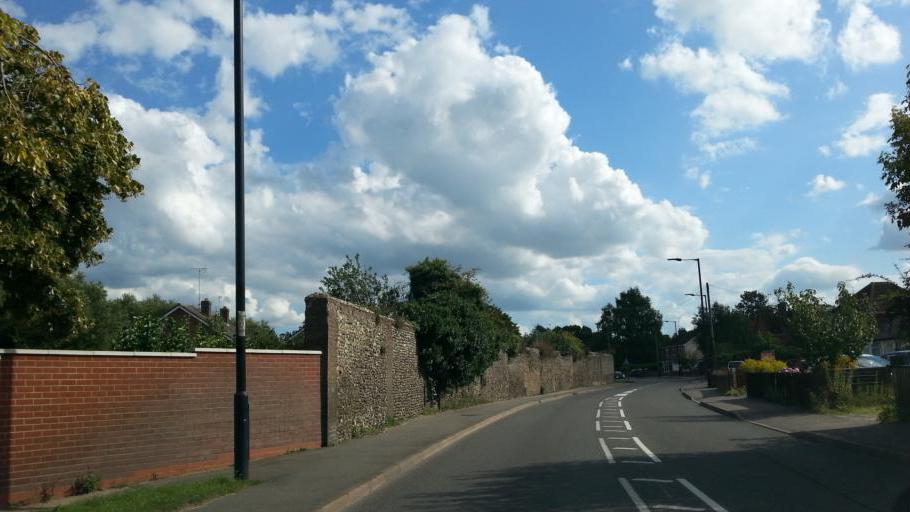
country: GB
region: England
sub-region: Suffolk
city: Bury St Edmunds
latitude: 52.2627
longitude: 0.7094
